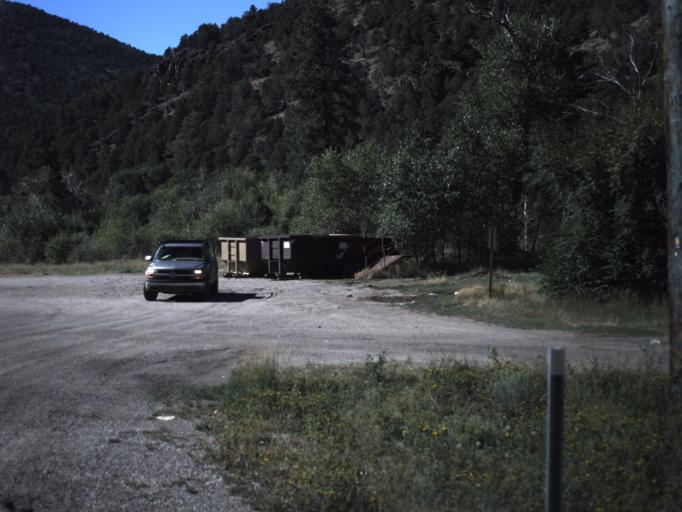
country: US
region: Utah
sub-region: Beaver County
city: Beaver
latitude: 38.2636
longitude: -112.5474
